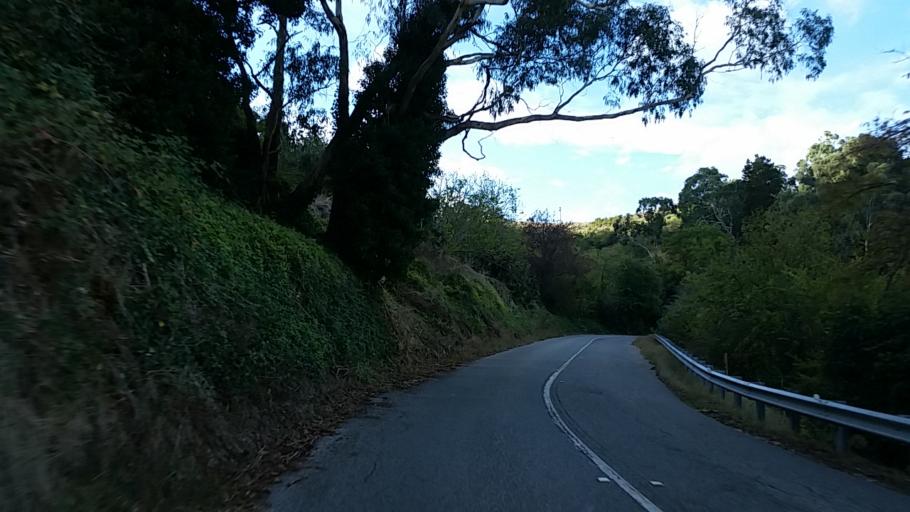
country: AU
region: South Australia
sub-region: Adelaide Hills
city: Adelaide Hills
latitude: -34.8889
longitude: 138.7418
